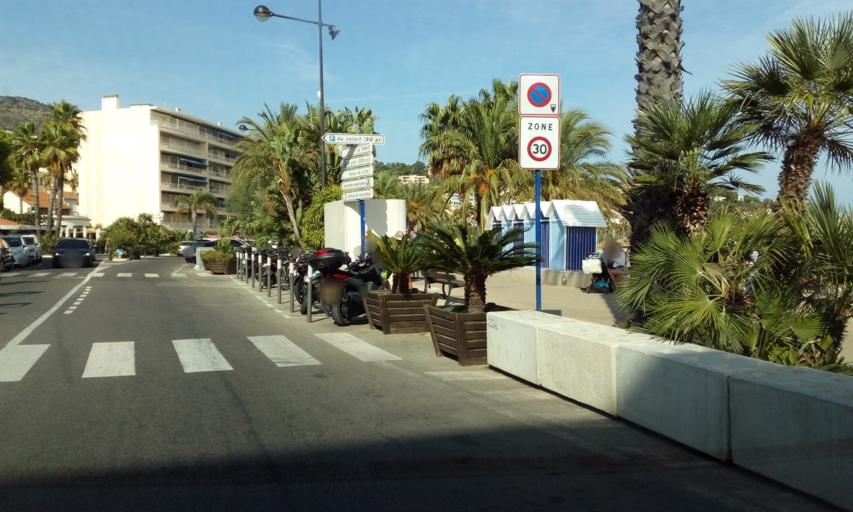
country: FR
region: Provence-Alpes-Cote d'Azur
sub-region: Departement du Var
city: Le Lavandou
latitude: 43.1364
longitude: 6.3674
